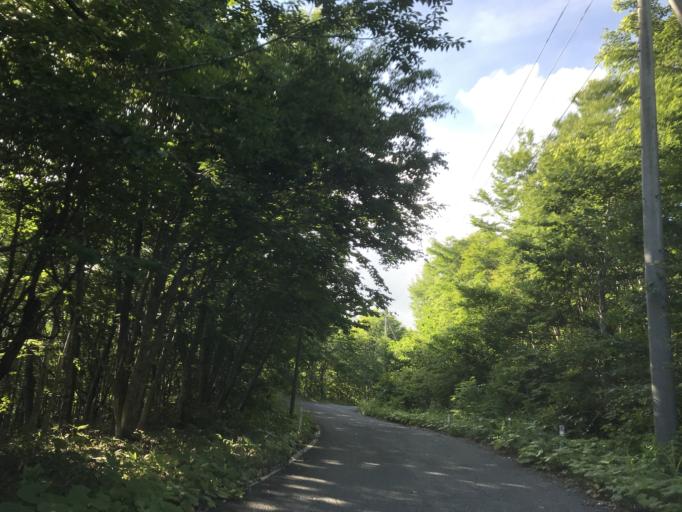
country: JP
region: Iwate
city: Ichinoseki
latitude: 38.9252
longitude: 140.8342
